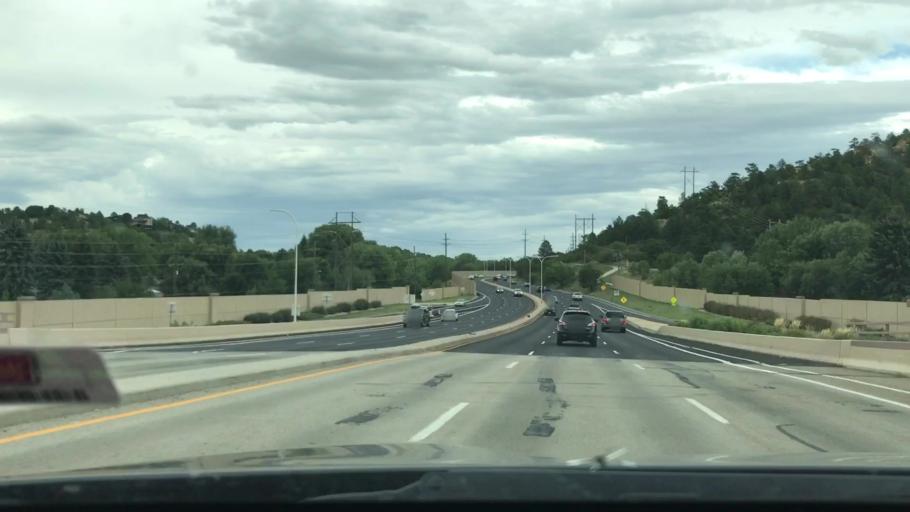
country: US
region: Colorado
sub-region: El Paso County
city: Colorado Springs
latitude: 38.8891
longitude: -104.7845
